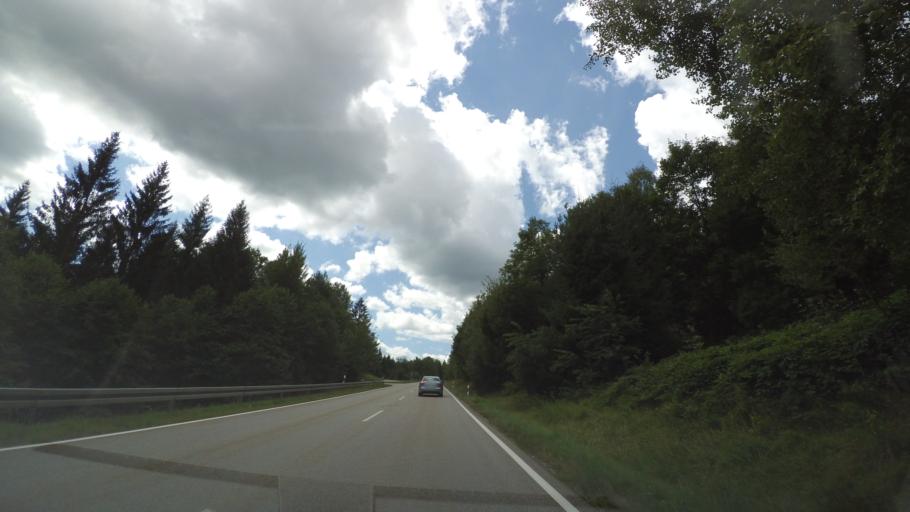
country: DE
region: Bavaria
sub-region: Lower Bavaria
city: Bodenmais
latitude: 49.0629
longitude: 13.0703
